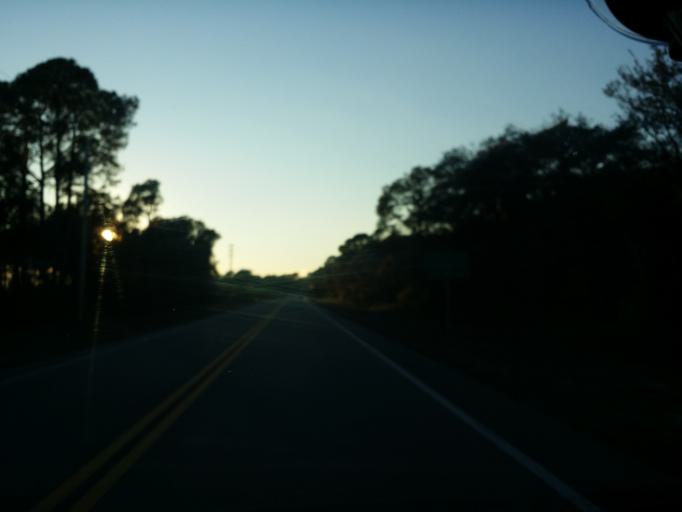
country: US
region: Florida
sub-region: Franklin County
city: Carrabelle
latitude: 29.9182
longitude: -84.5083
